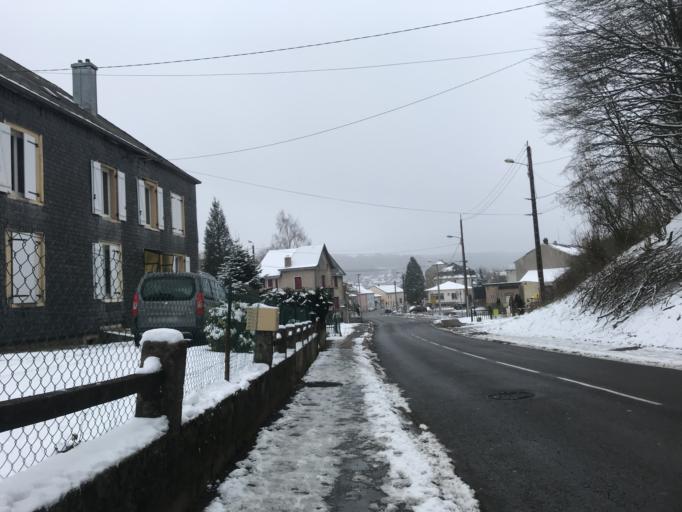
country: FR
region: Lorraine
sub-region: Departement de la Moselle
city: Russange
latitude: 49.4829
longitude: 5.9520
